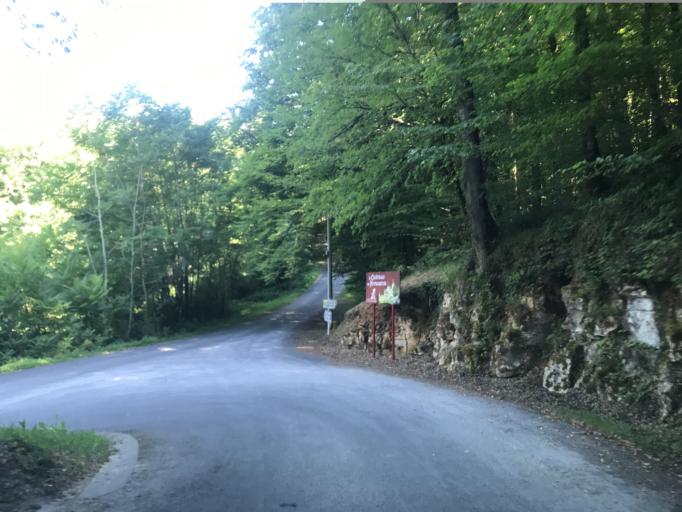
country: FR
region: Aquitaine
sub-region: Departement de la Dordogne
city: Sarlat-la-Caneda
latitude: 44.9114
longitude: 1.1404
